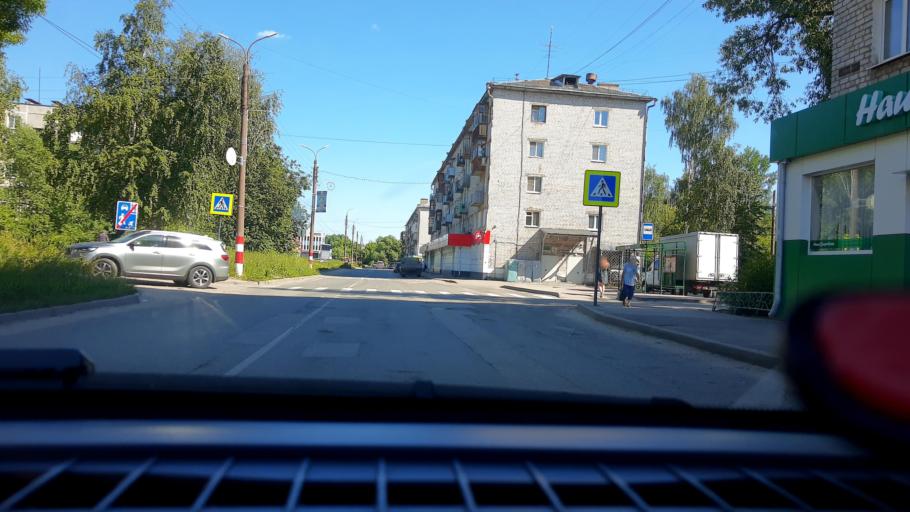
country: RU
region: Nizjnij Novgorod
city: Gidrotorf
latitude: 56.5183
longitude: 43.5550
